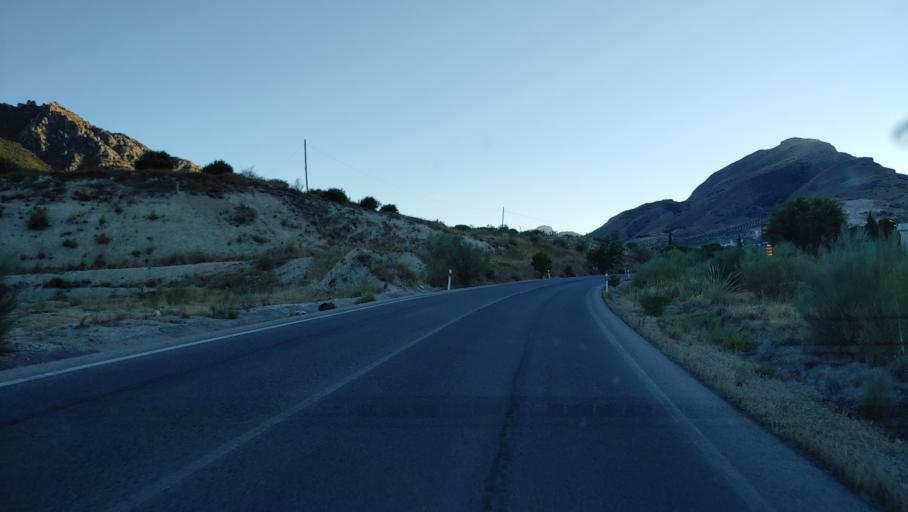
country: ES
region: Andalusia
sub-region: Provincia de Jaen
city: Jodar
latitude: 37.8291
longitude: -3.3533
